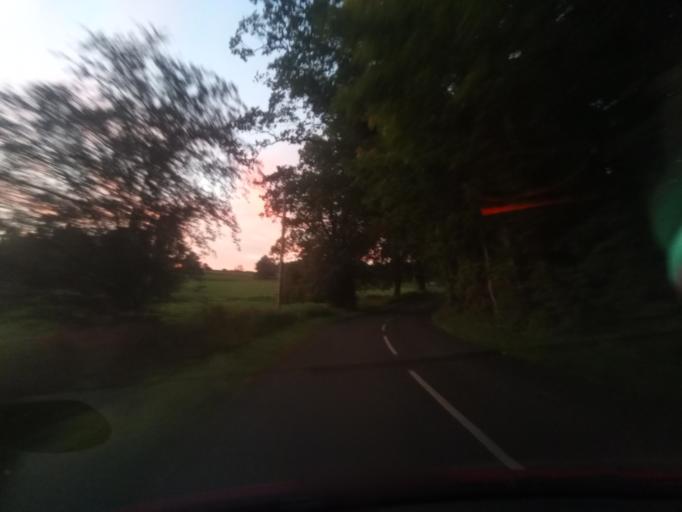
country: GB
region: England
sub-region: Northumberland
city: Wall
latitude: 55.0239
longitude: -2.1513
